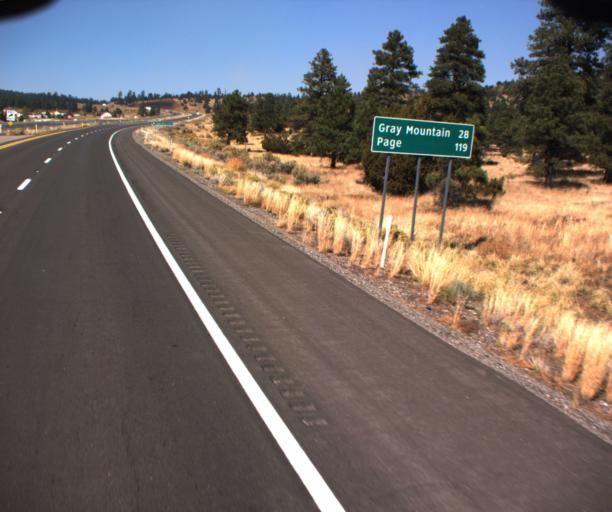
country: US
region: Arizona
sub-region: Coconino County
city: Flagstaff
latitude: 35.3421
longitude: -111.5592
